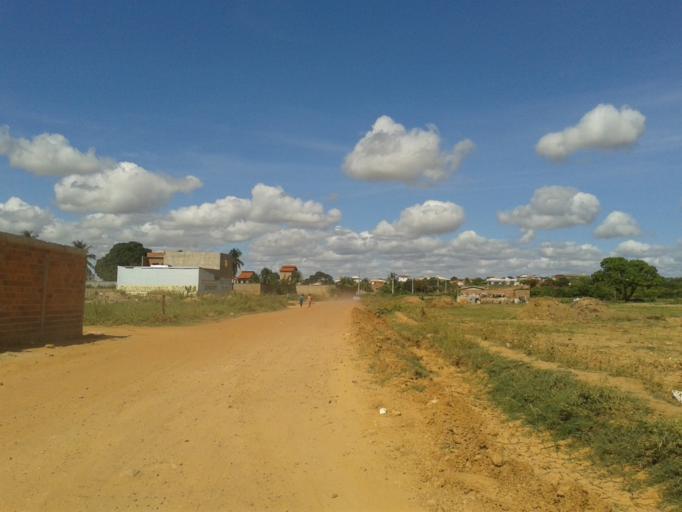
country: BR
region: Bahia
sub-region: Livramento Do Brumado
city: Livramento do Brumado
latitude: -13.6522
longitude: -41.8445
